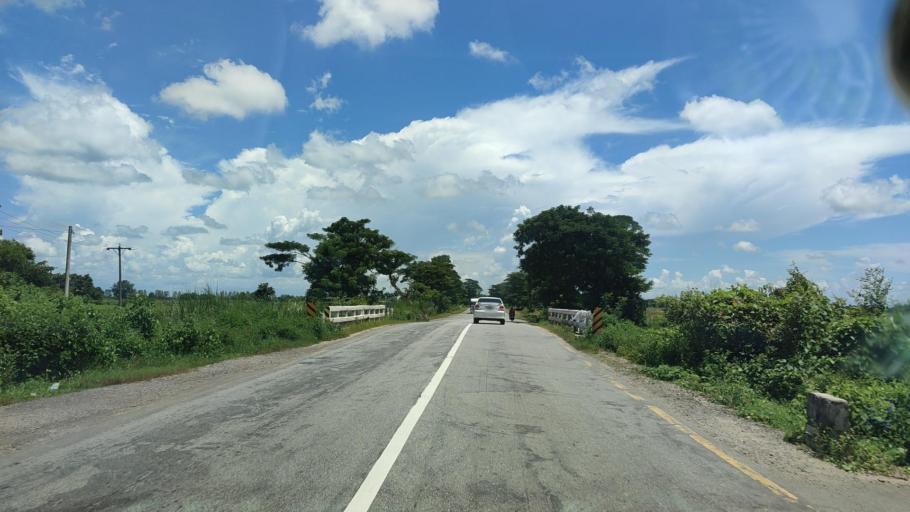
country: MM
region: Bago
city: Nyaunglebin
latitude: 18.1814
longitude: 96.5950
